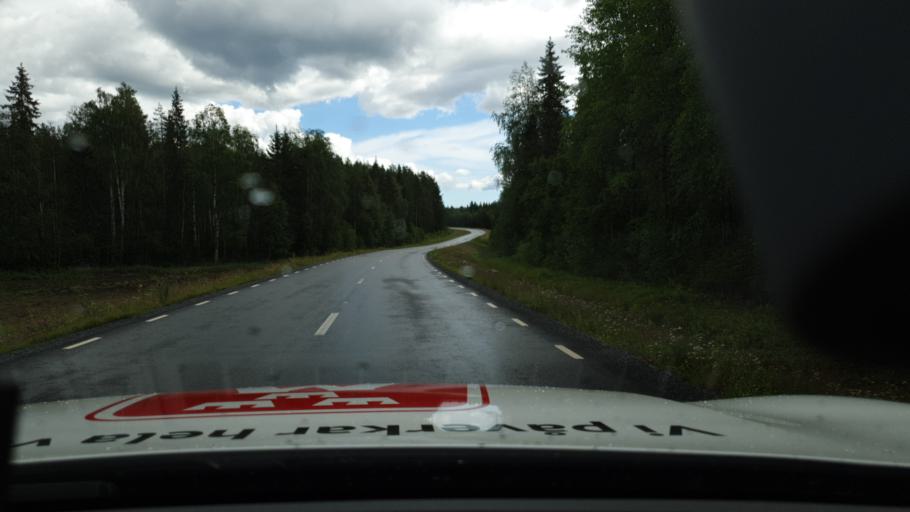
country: SE
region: Norrbotten
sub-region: Bodens Kommun
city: Saevast
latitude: 65.8390
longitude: 21.8244
